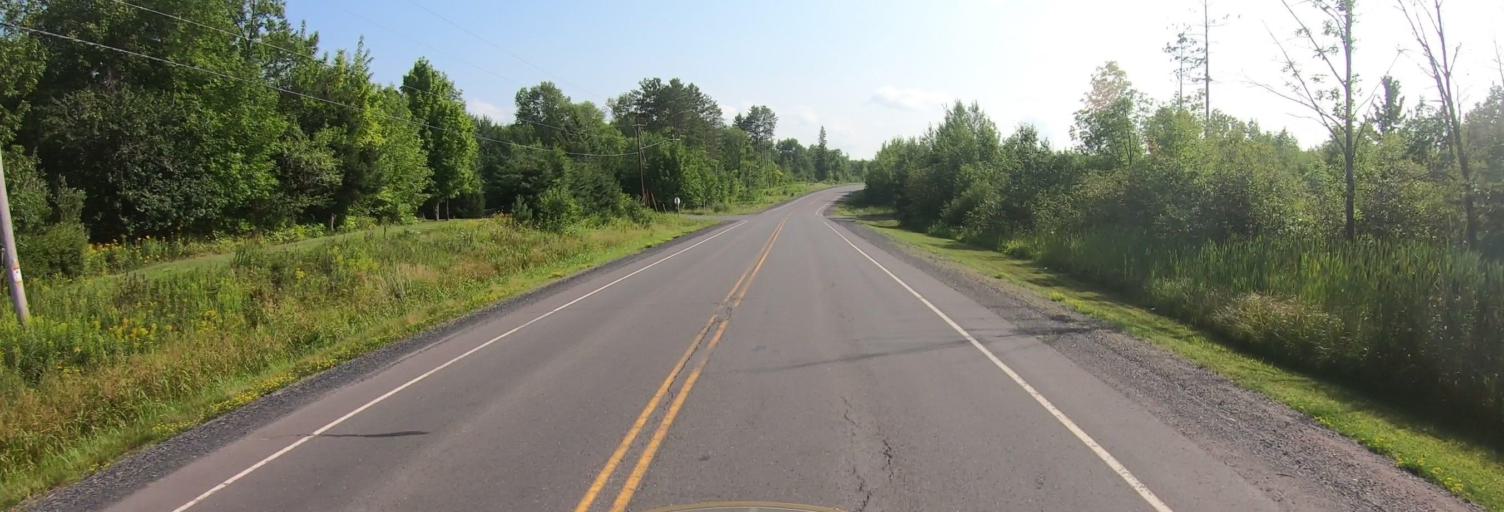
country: US
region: Wisconsin
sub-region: Iron County
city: Hurley
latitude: 46.4248
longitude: -90.2594
